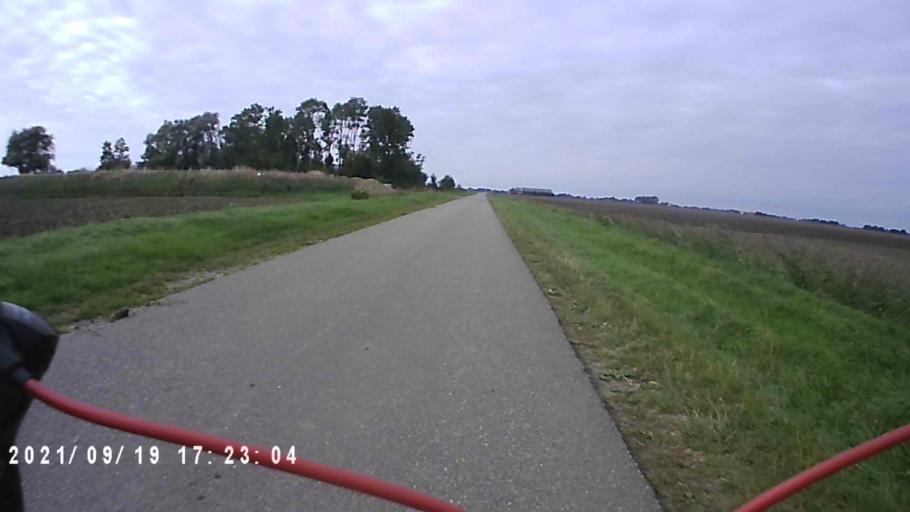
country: NL
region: Groningen
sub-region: Gemeente  Oldambt
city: Winschoten
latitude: 53.2128
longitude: 7.0176
